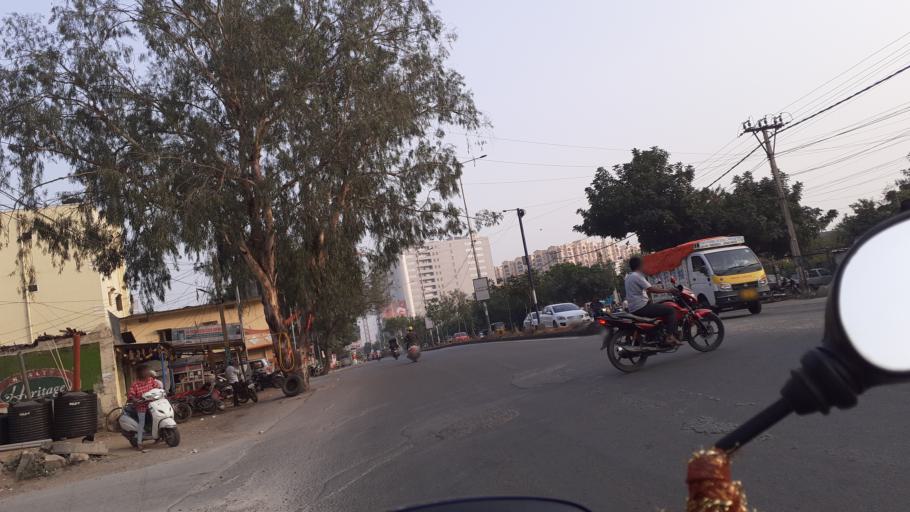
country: IN
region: Telangana
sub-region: Medak
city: Serilingampalle
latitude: 17.4883
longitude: 78.3555
